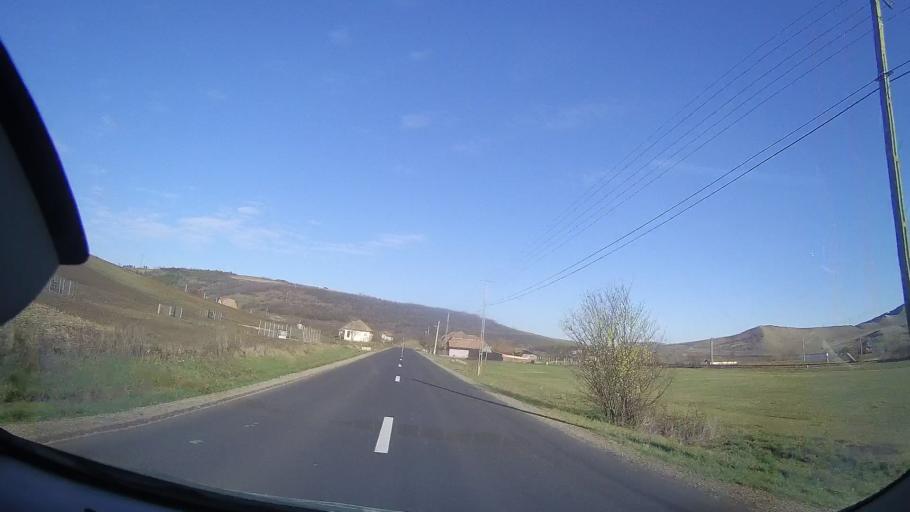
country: RO
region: Mures
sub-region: Comuna Zau De Campie
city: Zau de Campie
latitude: 46.6337
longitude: 24.1340
